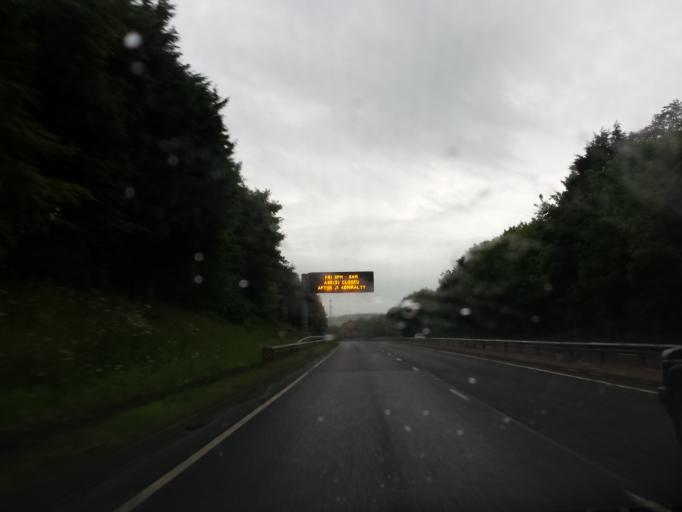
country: GB
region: Scotland
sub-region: Perth and Kinross
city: Perth
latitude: 56.3957
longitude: -3.4893
